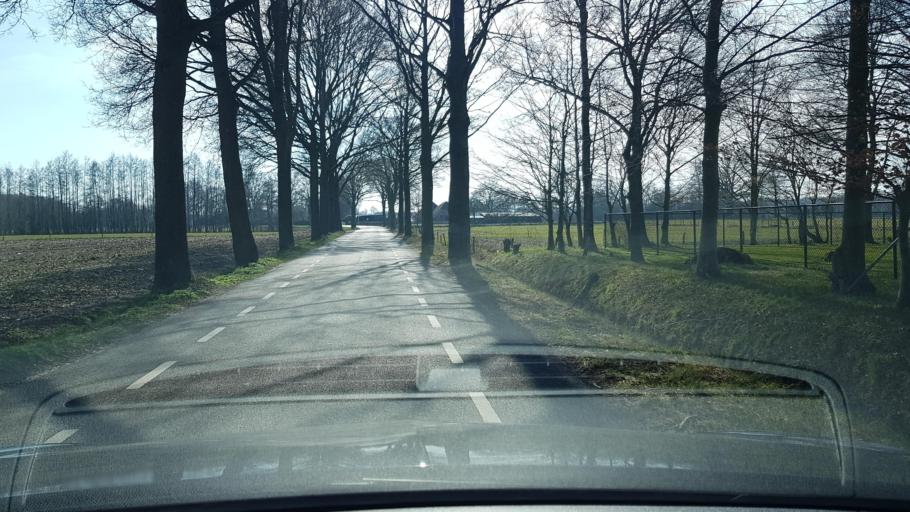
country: NL
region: Gelderland
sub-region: Gemeente Epe
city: Emst
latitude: 52.3130
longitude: 5.9526
